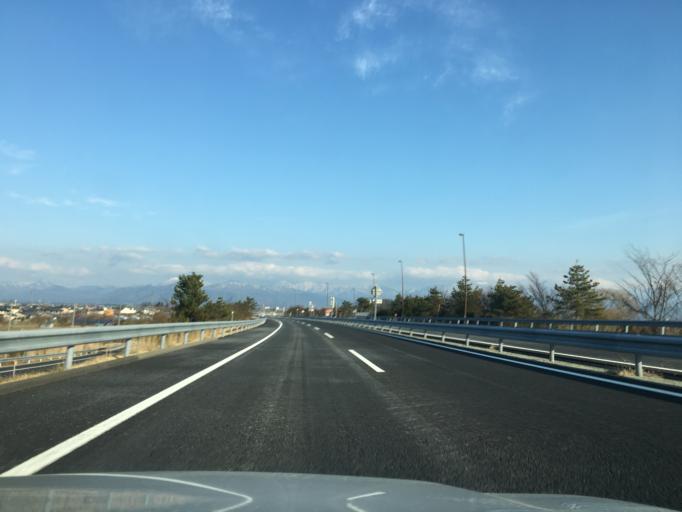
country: JP
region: Yamagata
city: Sagae
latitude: 38.3675
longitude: 140.2554
